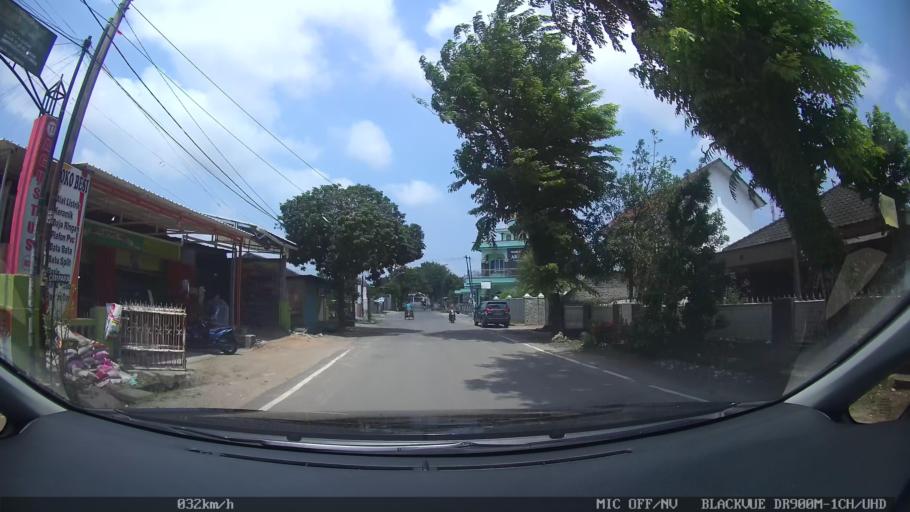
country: ID
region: Lampung
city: Kedaton
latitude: -5.3695
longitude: 105.2694
